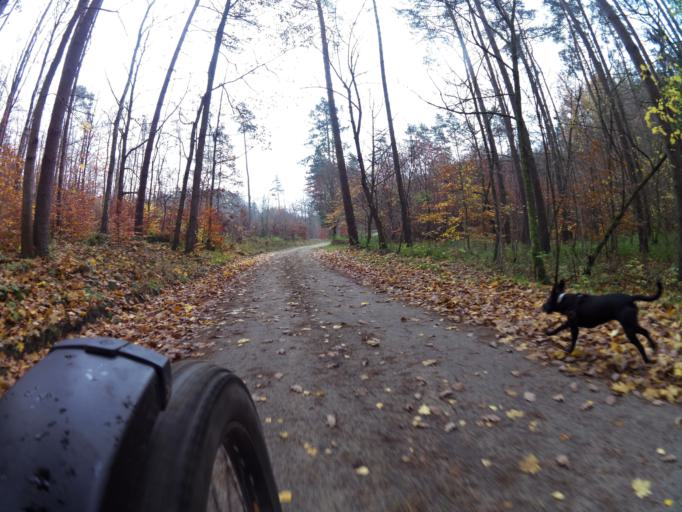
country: PL
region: Pomeranian Voivodeship
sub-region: Powiat pucki
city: Krokowa
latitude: 54.7796
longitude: 18.0913
